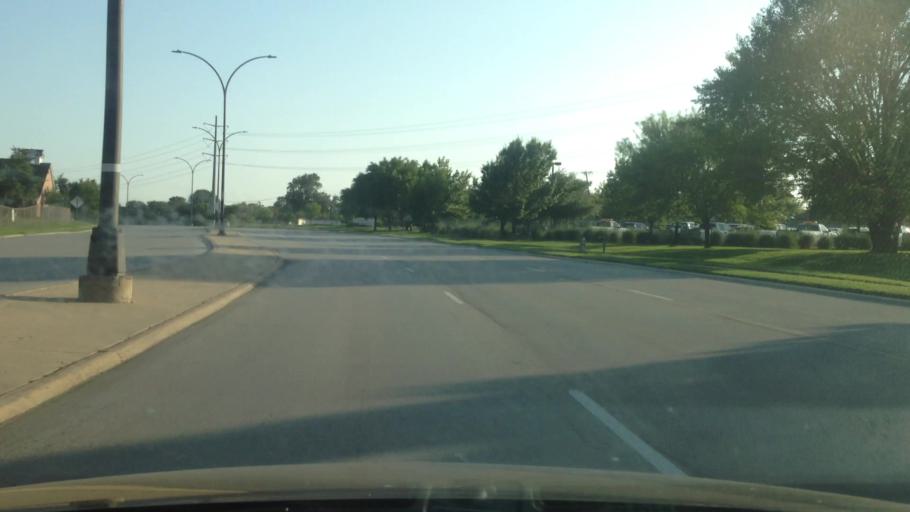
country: US
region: Texas
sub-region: Tarrant County
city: Pantego
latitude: 32.7116
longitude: -97.1898
